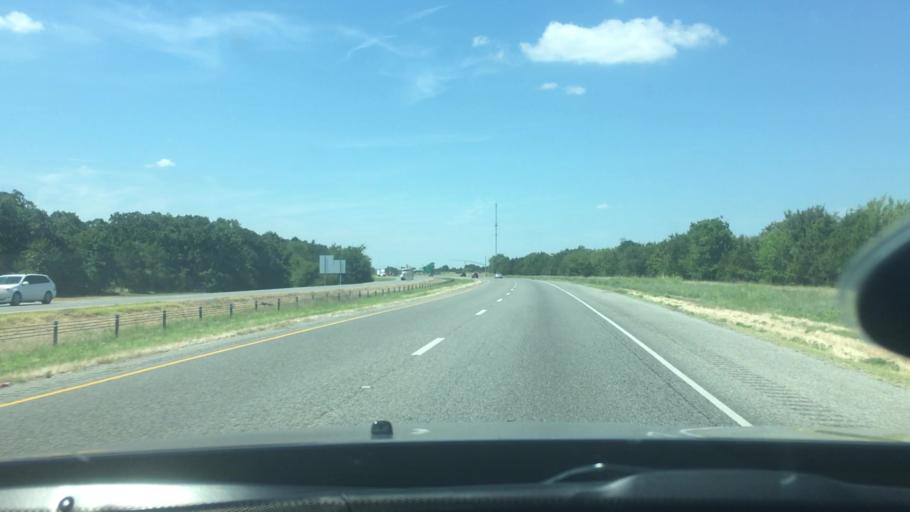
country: US
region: Oklahoma
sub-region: Bryan County
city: Colbert
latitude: 33.8747
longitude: -96.5050
